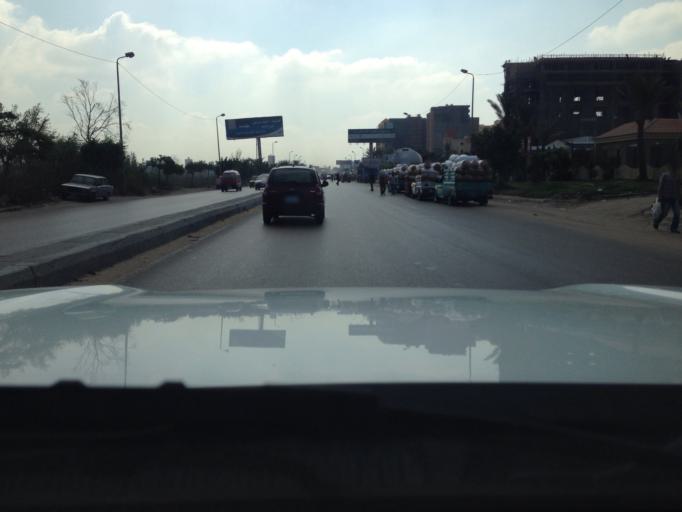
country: EG
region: Alexandria
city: Alexandria
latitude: 31.2038
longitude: 29.9802
